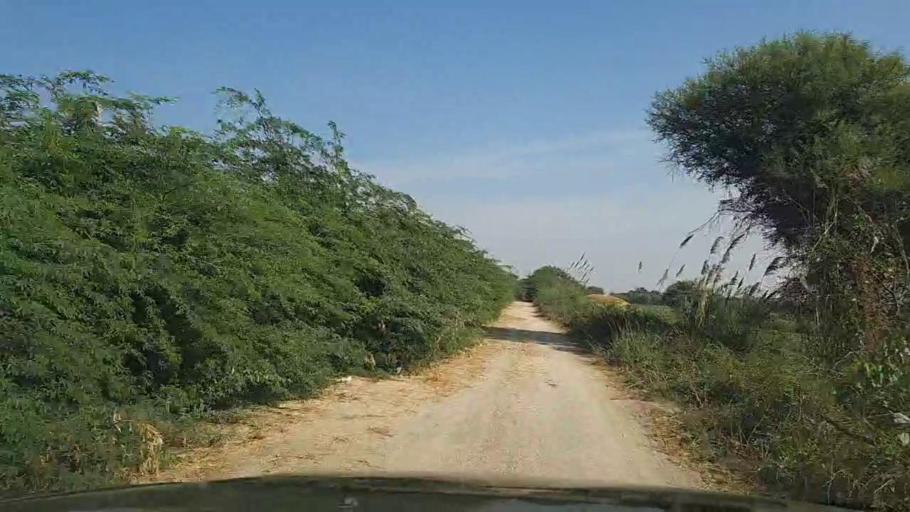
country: PK
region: Sindh
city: Thatta
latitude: 24.7115
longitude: 67.7875
